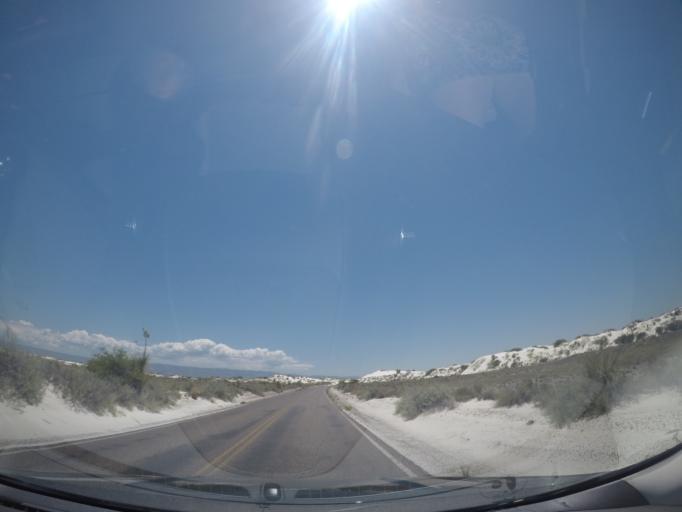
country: US
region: New Mexico
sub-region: Otero County
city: Holloman Air Force Base
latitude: 32.7971
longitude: -106.2207
